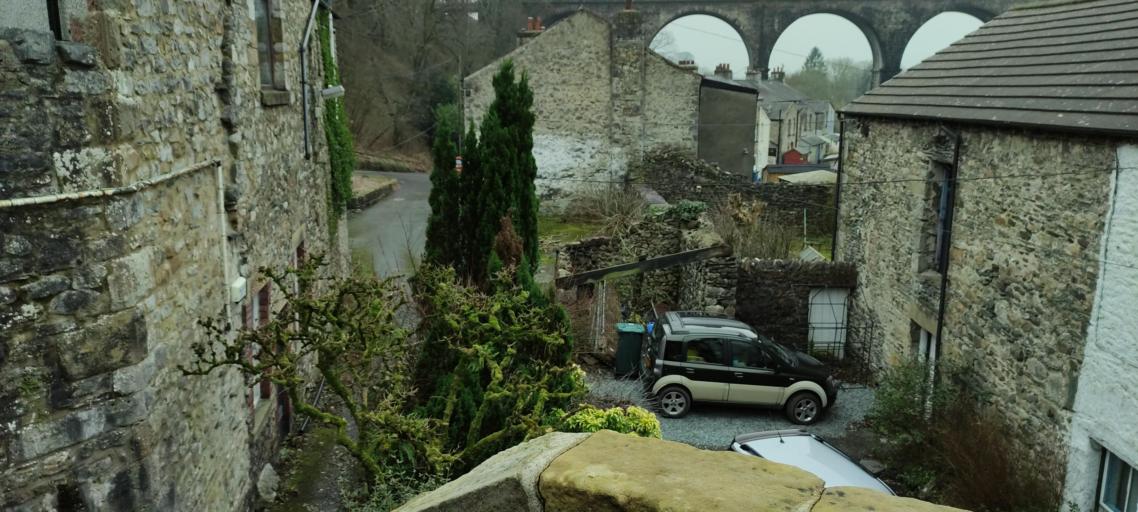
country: GB
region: England
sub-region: North Yorkshire
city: Ingleton
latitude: 54.1538
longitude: -2.4694
